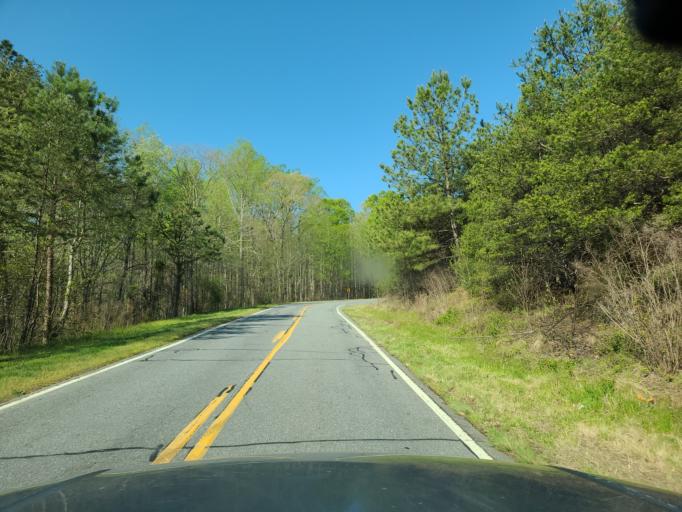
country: US
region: North Carolina
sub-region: Rutherford County
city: Spindale
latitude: 35.4028
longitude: -81.8776
